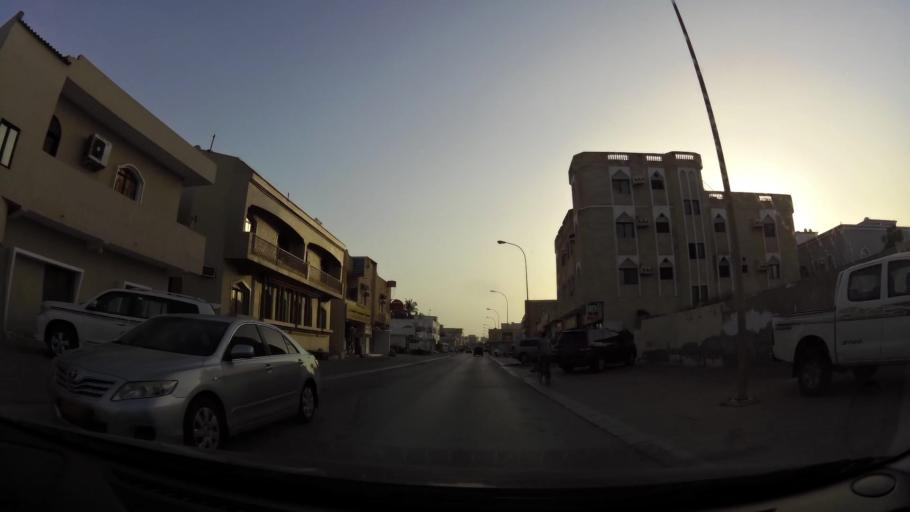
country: OM
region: Zufar
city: Salalah
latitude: 17.0161
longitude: 54.1152
